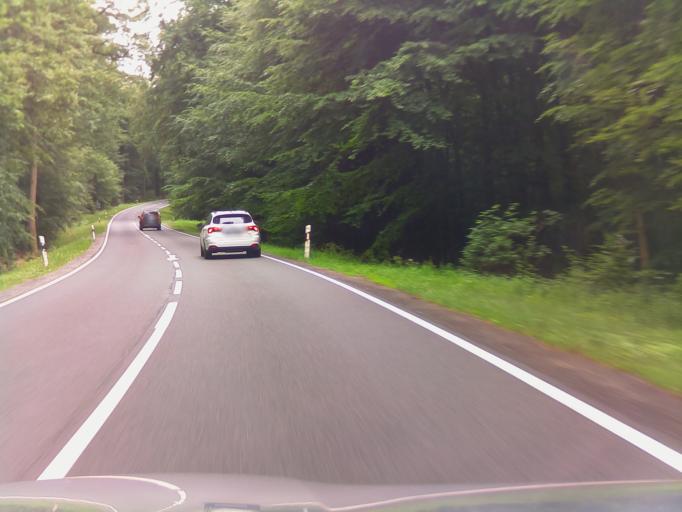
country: DE
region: Bavaria
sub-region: Regierungsbezirk Unterfranken
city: Weibersbrunn
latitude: 49.9587
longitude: 9.3526
